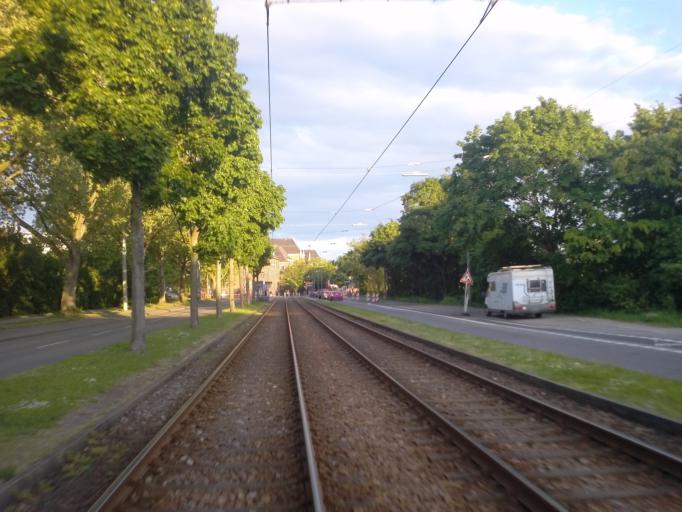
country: DE
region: Baden-Wuerttemberg
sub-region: Karlsruhe Region
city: Karlsruhe
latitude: 49.0209
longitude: 8.3625
